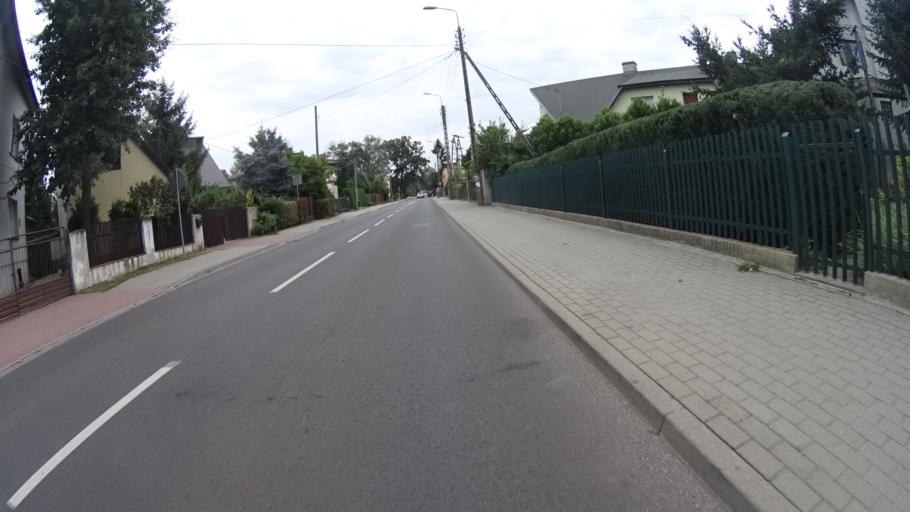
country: PL
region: Masovian Voivodeship
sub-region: Powiat pruszkowski
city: Granica
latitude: 52.1436
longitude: 20.7915
